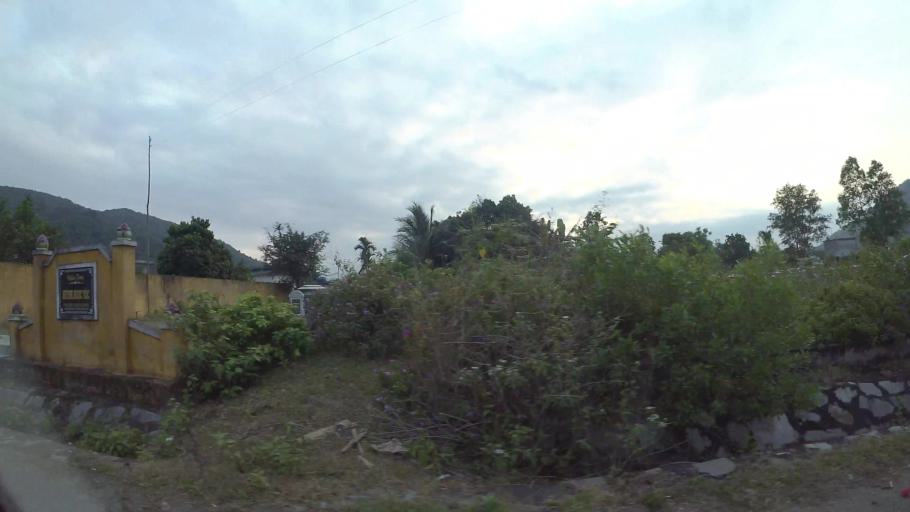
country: VN
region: Da Nang
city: Lien Chieu
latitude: 16.0581
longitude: 108.1245
